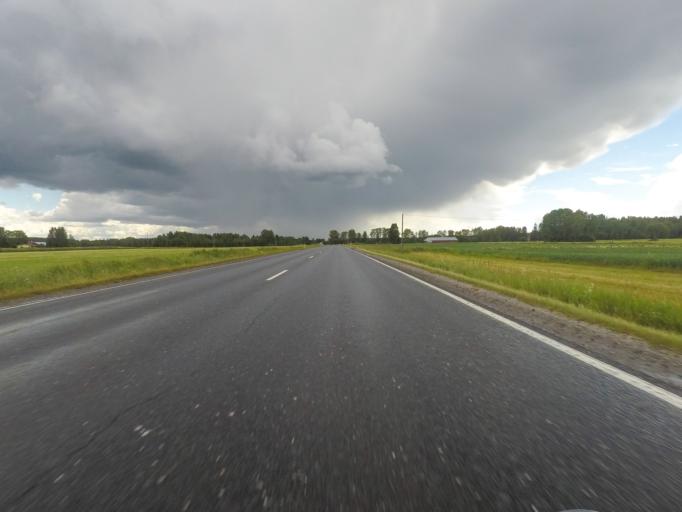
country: FI
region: Paijanne Tavastia
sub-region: Lahti
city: Hartola
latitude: 61.6176
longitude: 26.0085
